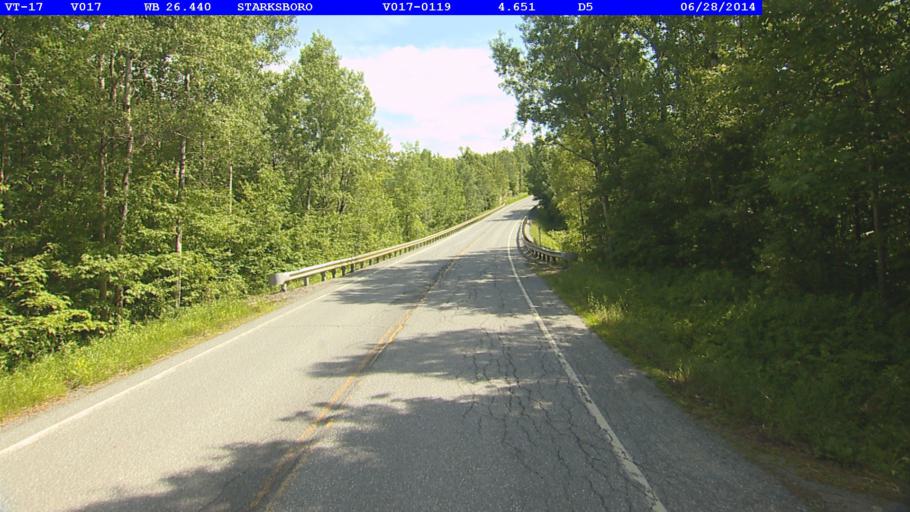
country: US
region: Vermont
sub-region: Addison County
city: Bristol
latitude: 44.2062
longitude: -72.9649
